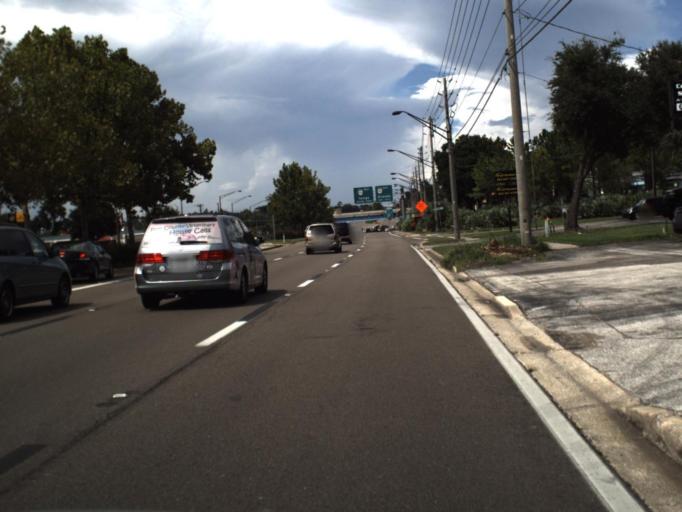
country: US
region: Florida
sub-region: Polk County
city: Medulla
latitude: 27.9919
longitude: -81.9567
